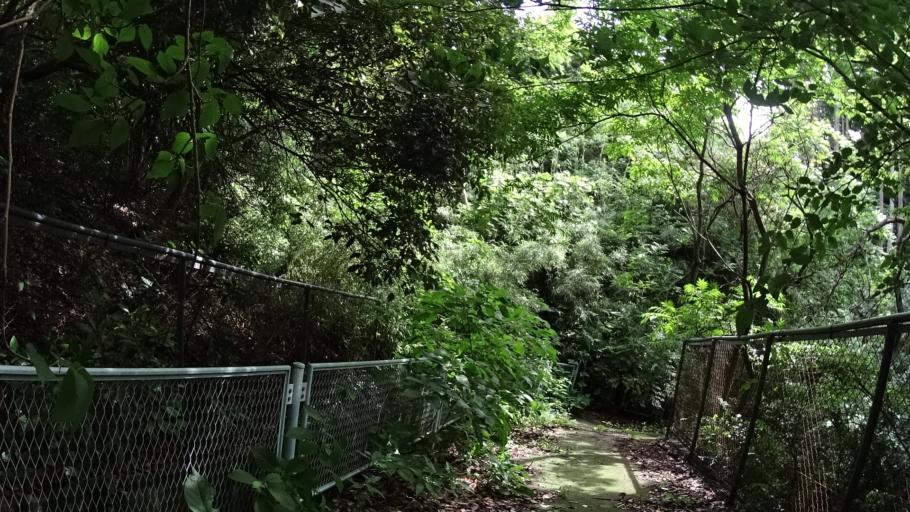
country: JP
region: Kanagawa
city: Yokosuka
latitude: 35.2693
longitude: 139.6337
